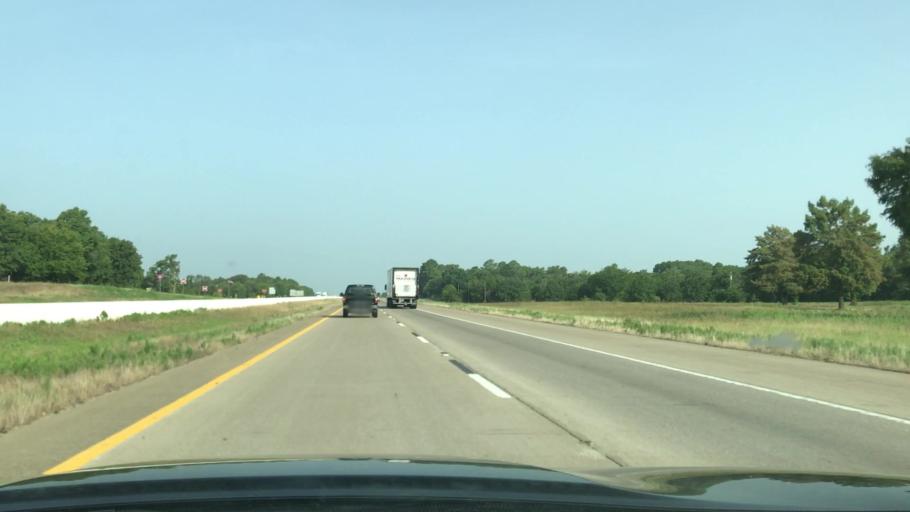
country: US
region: Texas
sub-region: Van Zandt County
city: Canton
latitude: 32.6080
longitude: -95.9512
